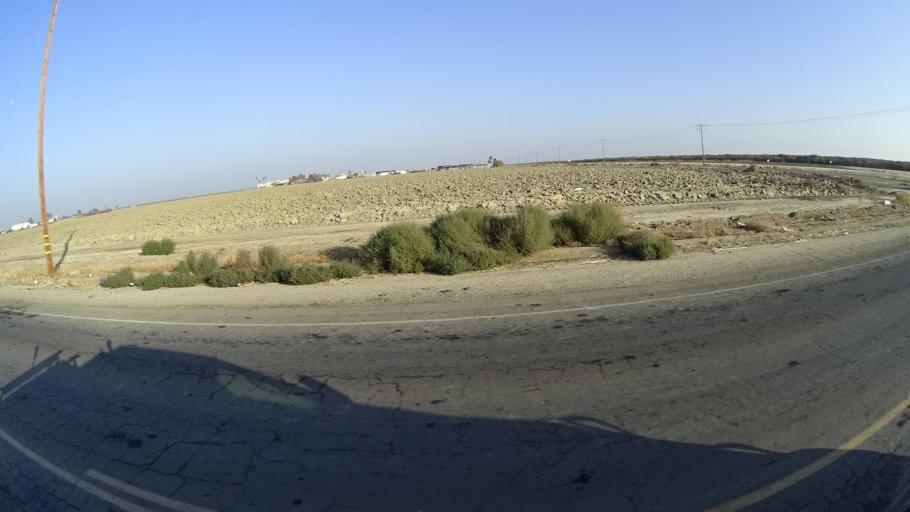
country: US
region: California
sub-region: Kern County
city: Delano
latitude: 35.7906
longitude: -119.1796
